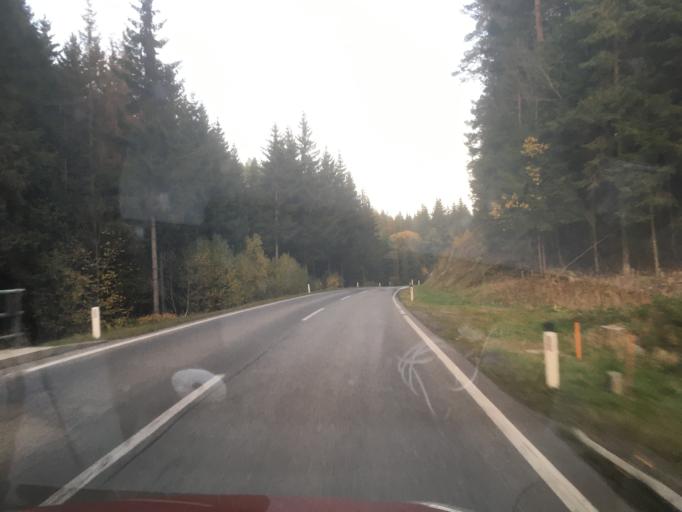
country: AT
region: Lower Austria
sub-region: Politischer Bezirk Zwettl
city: Langschlag
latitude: 48.5797
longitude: 14.8656
